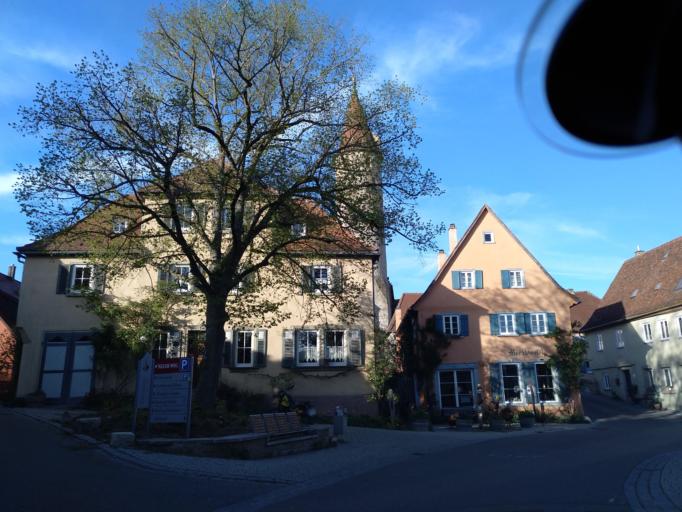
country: DE
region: Baden-Wuerttemberg
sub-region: Regierungsbezirk Stuttgart
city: Kirchberg an der Jagst
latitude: 49.2039
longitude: 9.9814
